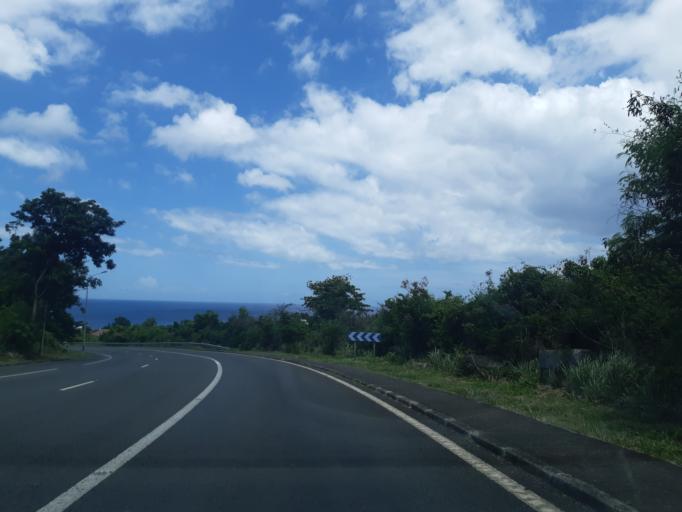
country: GP
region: Guadeloupe
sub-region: Guadeloupe
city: Basse-Terre
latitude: 15.9995
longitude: -61.7255
